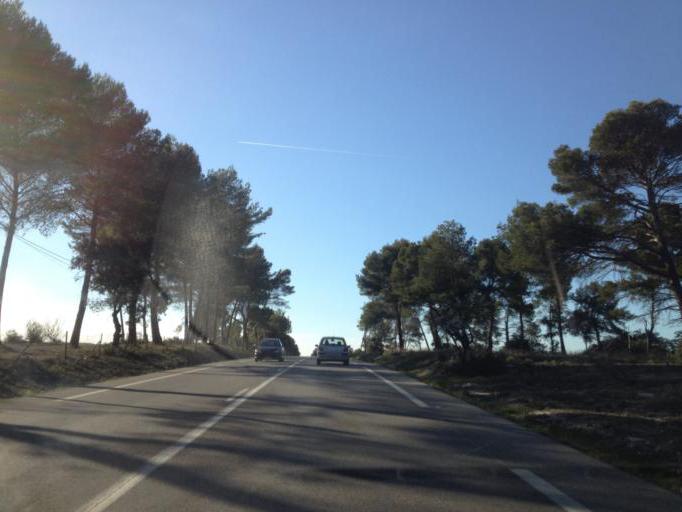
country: FR
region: Provence-Alpes-Cote d'Azur
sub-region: Departement des Bouches-du-Rhone
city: Eguilles
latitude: 43.6013
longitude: 5.3445
